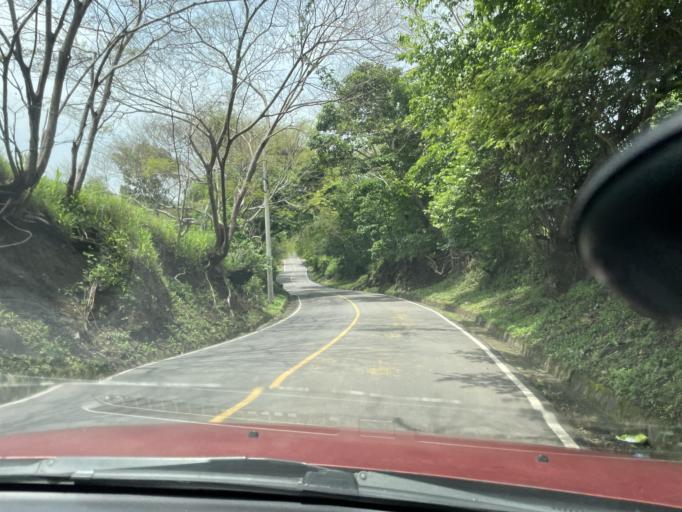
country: SV
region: La Union
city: Santa Rosa de Lima
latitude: 13.6516
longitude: -87.8359
